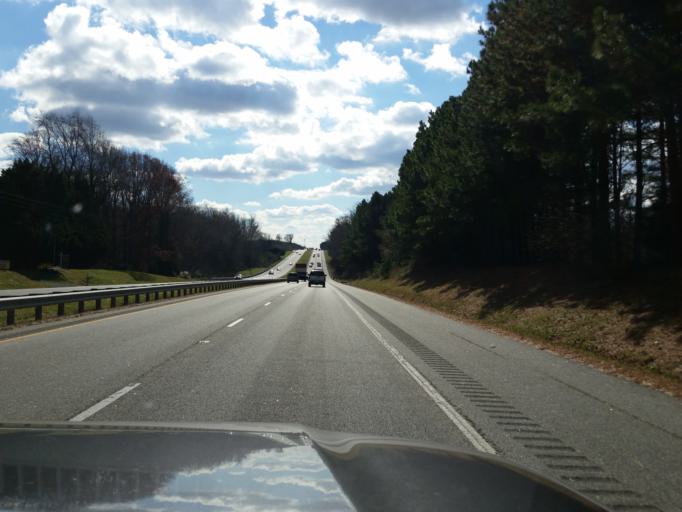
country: US
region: Maryland
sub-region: Queen Anne's County
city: Centreville
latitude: 38.9186
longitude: -76.0623
